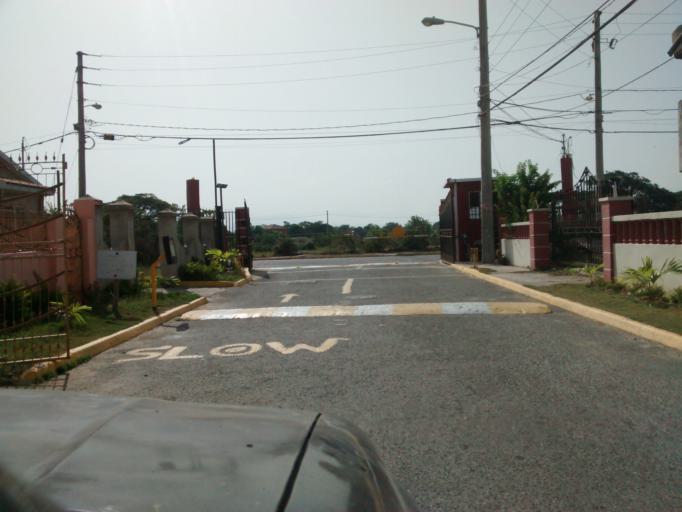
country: JM
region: Saint Catherine
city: Portmore
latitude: 17.9865
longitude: -76.8835
